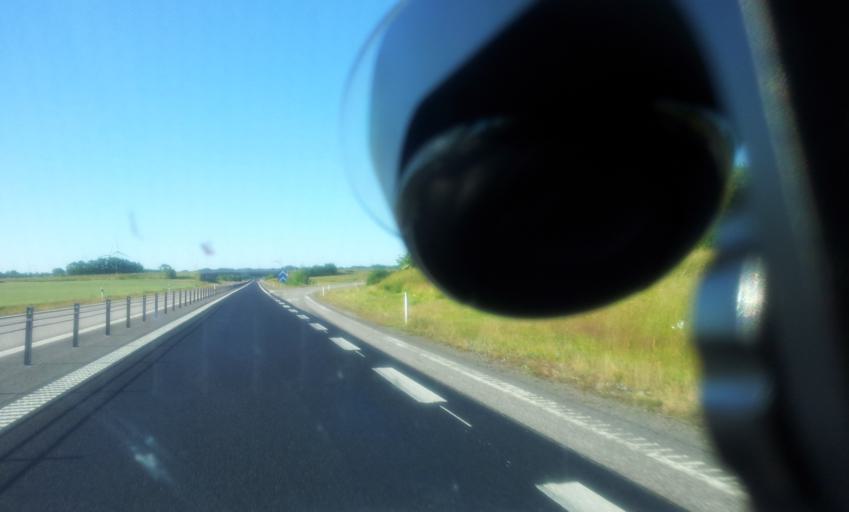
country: SE
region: Kalmar
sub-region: Torsas Kommun
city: Torsas
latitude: 56.4559
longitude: 16.0786
